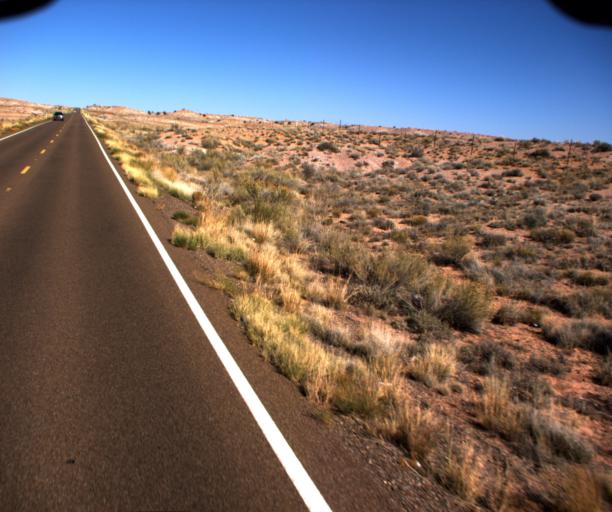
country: US
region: Arizona
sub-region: Navajo County
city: Dilkon
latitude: 35.2002
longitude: -110.4401
